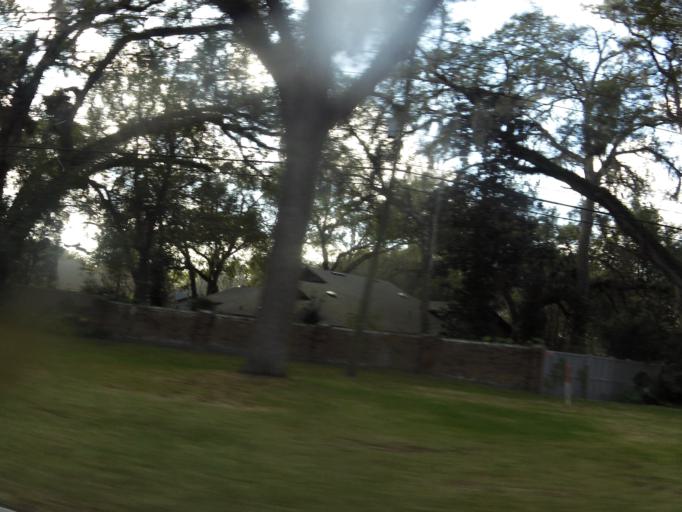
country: US
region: Florida
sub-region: Volusia County
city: North DeLand
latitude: 29.0839
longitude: -81.3201
